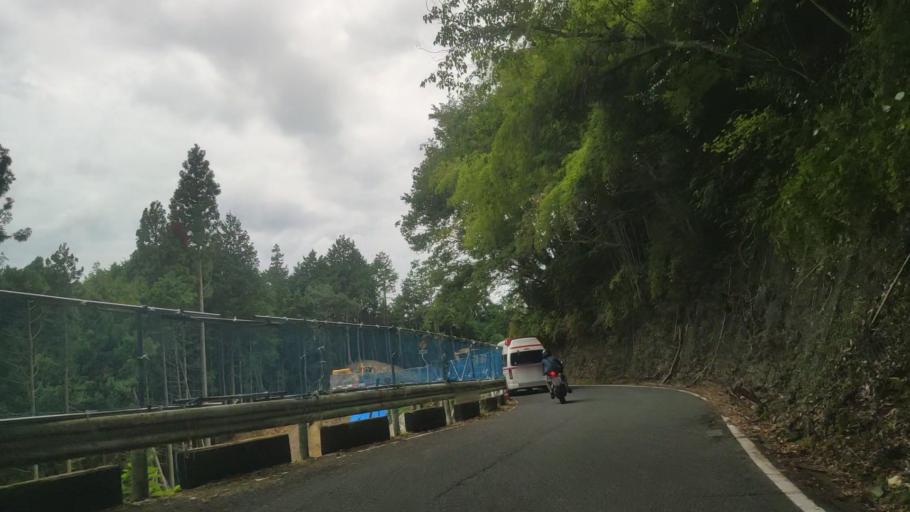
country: JP
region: Wakayama
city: Koya
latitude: 34.2246
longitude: 135.5393
